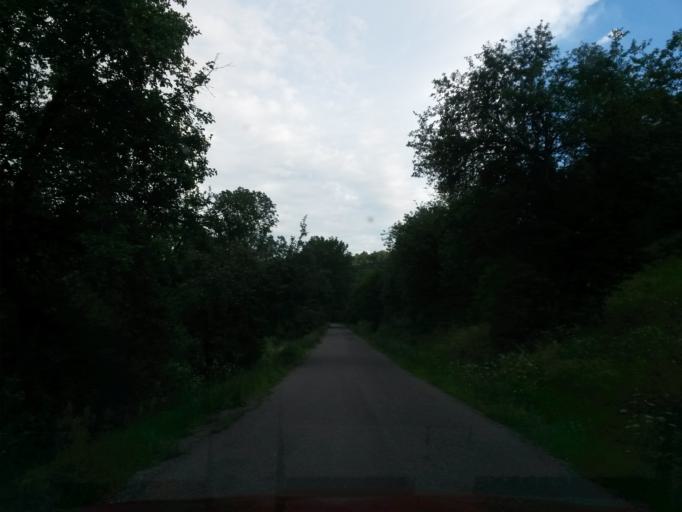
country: SK
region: Banskobystricky
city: Velky Krtis
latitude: 48.3096
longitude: 19.4599
